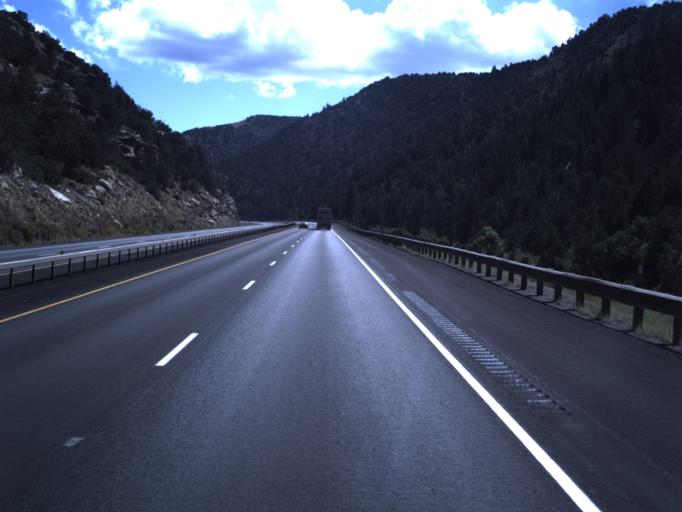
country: US
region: Utah
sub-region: Sevier County
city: Salina
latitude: 38.8887
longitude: -111.6113
